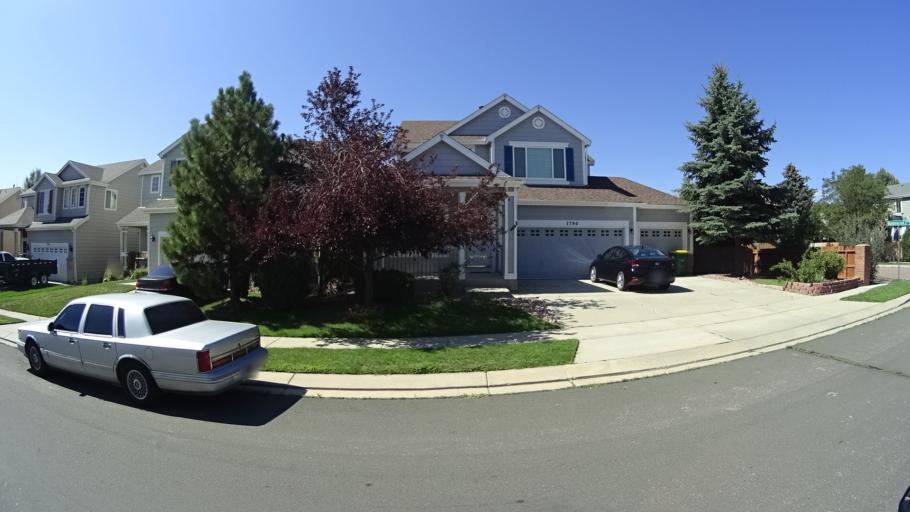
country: US
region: Colorado
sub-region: El Paso County
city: Black Forest
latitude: 38.9448
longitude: -104.7454
